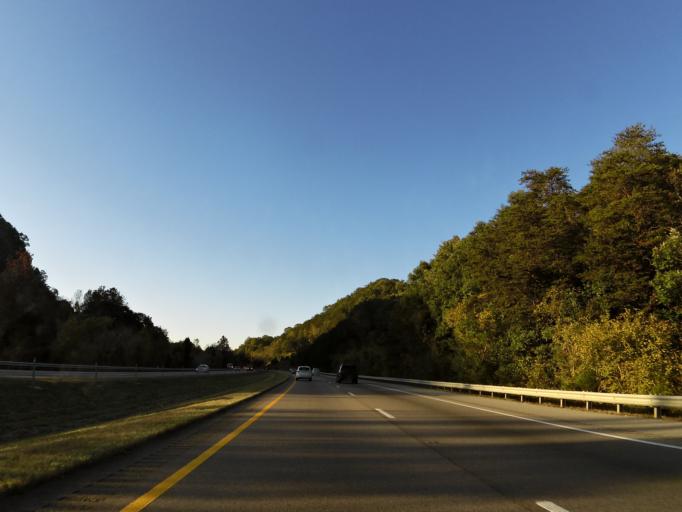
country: US
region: Tennessee
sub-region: Anderson County
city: Norris
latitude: 36.1302
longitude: -84.0363
